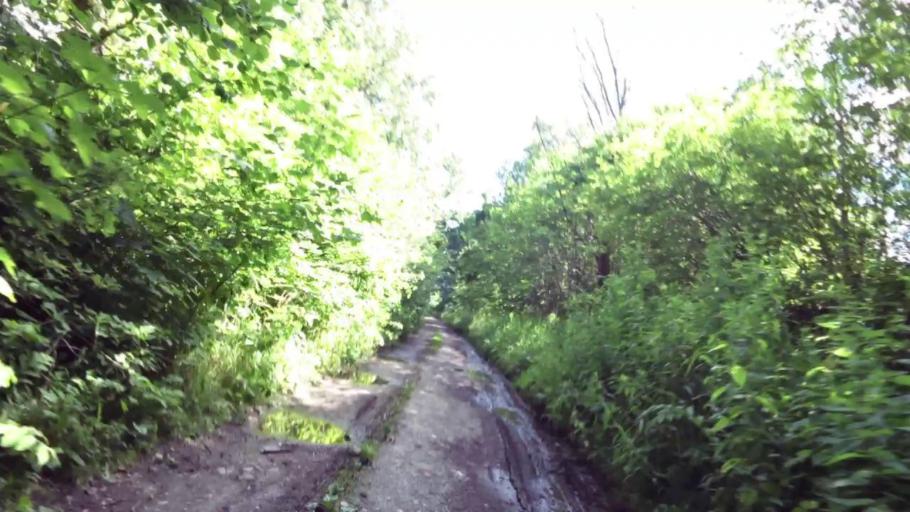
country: PL
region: West Pomeranian Voivodeship
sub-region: Powiat slawienski
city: Slawno
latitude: 54.5067
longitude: 16.7043
